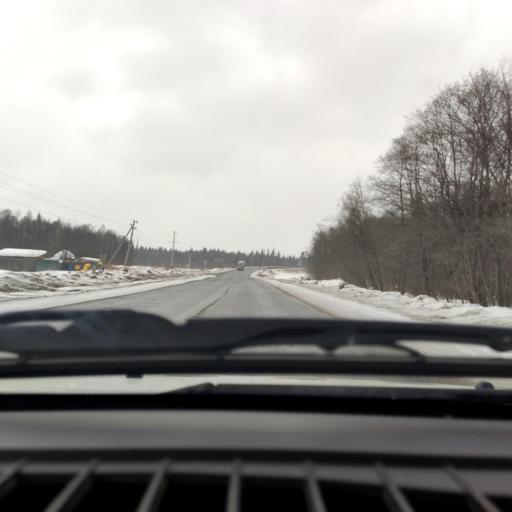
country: RU
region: Perm
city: Overyata
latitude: 58.1002
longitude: 55.8115
